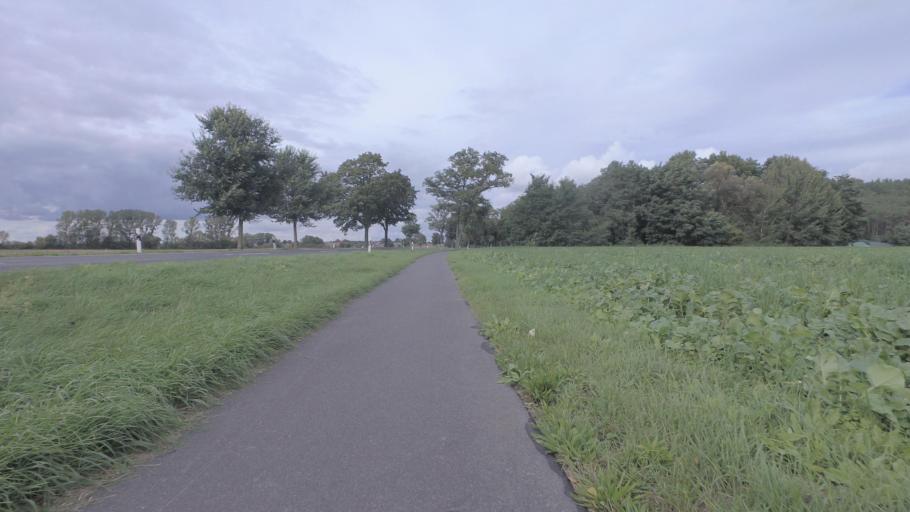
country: DE
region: Brandenburg
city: Trebbin
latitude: 52.1829
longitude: 13.1720
